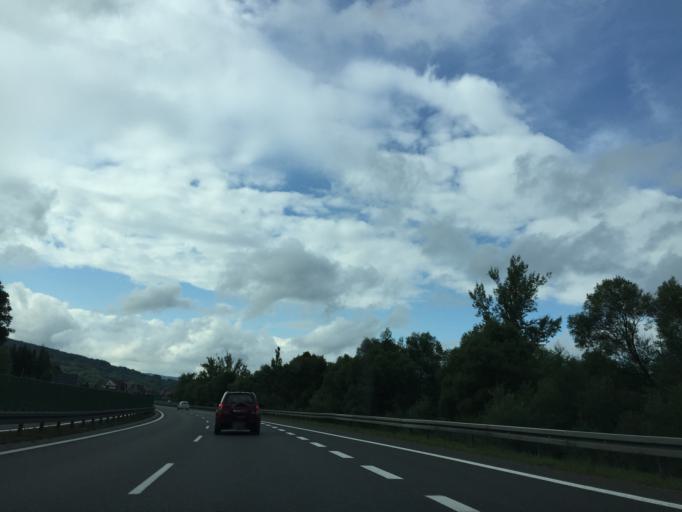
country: PL
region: Lesser Poland Voivodeship
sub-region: Powiat myslenicki
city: Pcim
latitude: 49.7537
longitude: 19.9705
